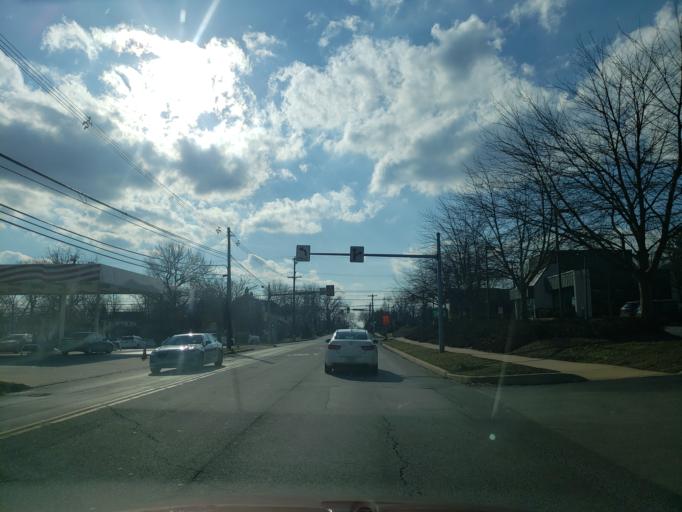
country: US
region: Pennsylvania
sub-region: Montgomery County
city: Norristown
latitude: 40.1504
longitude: -75.3091
